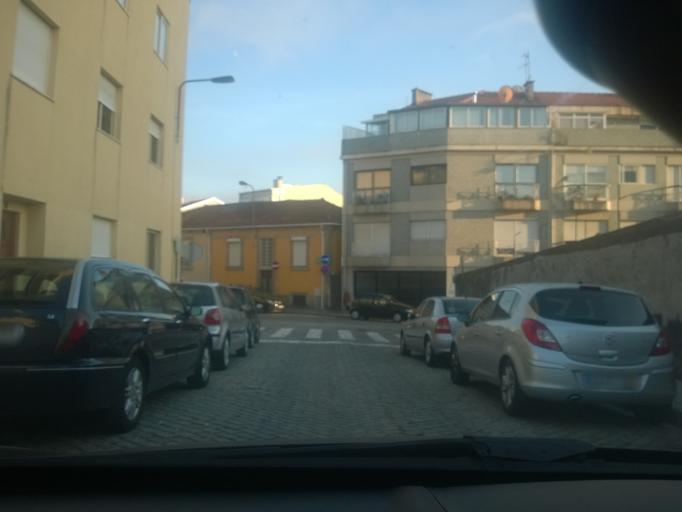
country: PT
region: Porto
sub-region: Porto
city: Porto
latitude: 41.1606
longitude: -8.6343
